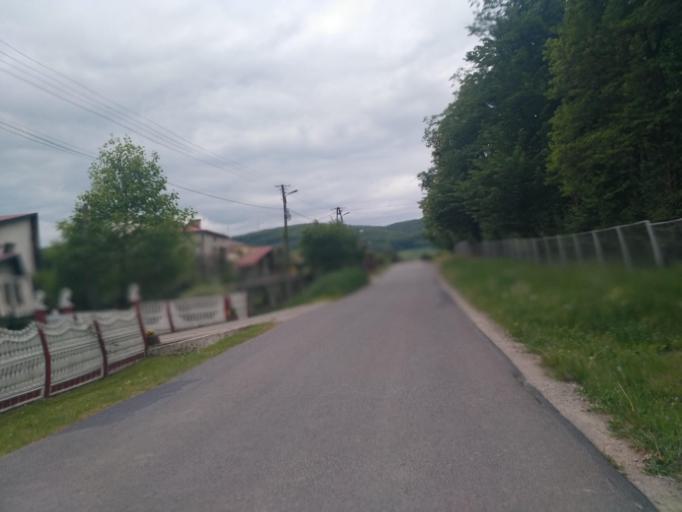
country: PL
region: Subcarpathian Voivodeship
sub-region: Powiat krosnienski
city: Jedlicze
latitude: 49.6937
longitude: 21.6386
